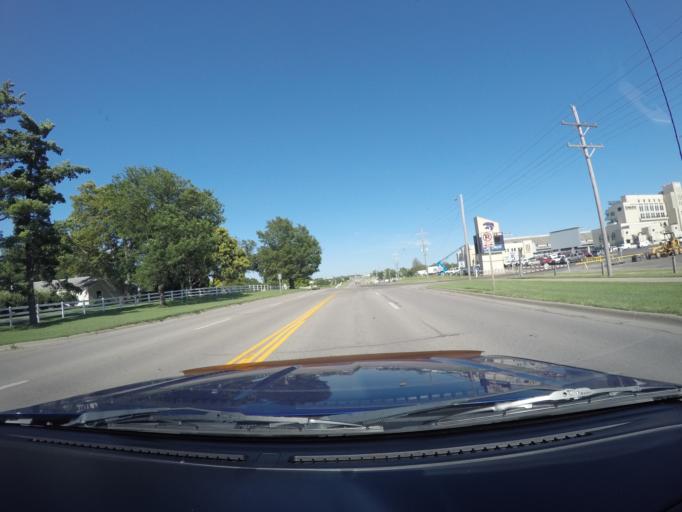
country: US
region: Kansas
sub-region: Riley County
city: Manhattan
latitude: 39.2039
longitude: -96.5965
